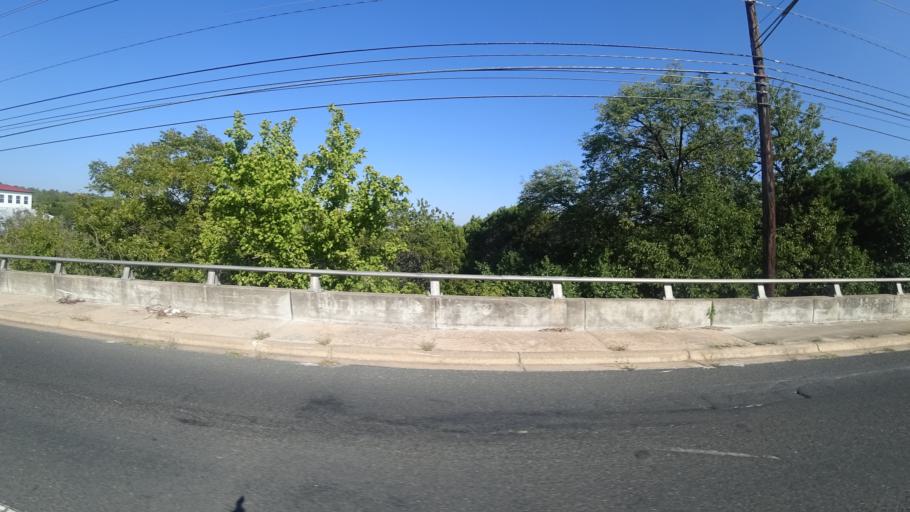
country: US
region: Texas
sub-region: Travis County
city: Wells Branch
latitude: 30.3642
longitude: -97.6684
